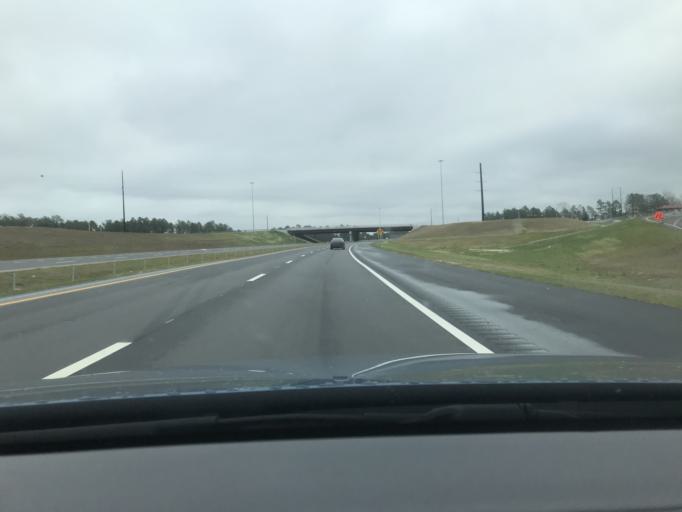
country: US
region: North Carolina
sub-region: Cumberland County
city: Fort Bragg
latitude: 35.1056
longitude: -79.0160
